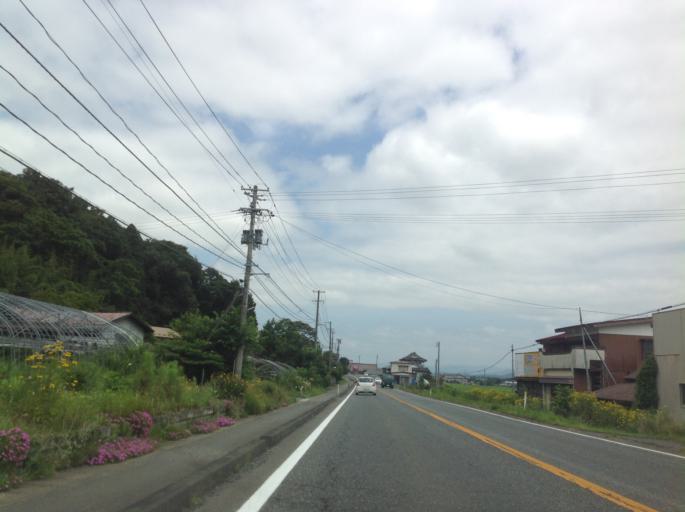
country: JP
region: Iwate
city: Mizusawa
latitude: 39.1078
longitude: 141.1404
